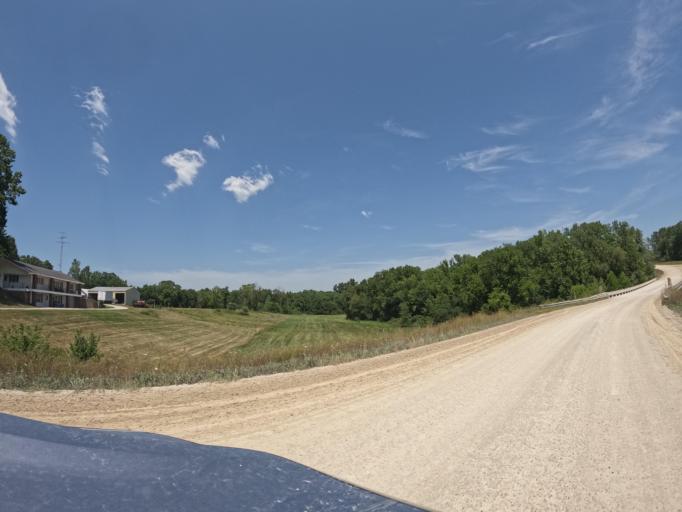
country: US
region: Iowa
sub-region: Henry County
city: Mount Pleasant
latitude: 40.9572
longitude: -91.5947
